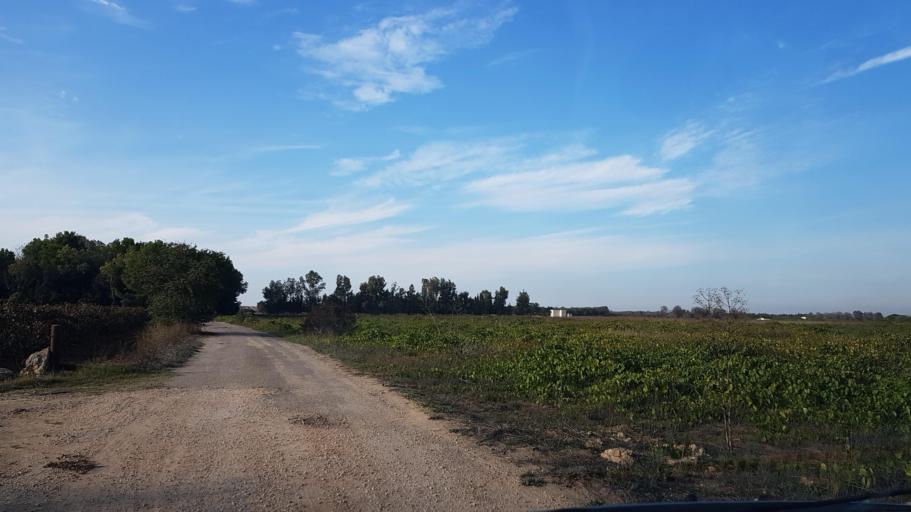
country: IT
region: Apulia
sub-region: Provincia di Brindisi
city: San Pancrazio Salentino
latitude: 40.4903
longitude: 17.8556
